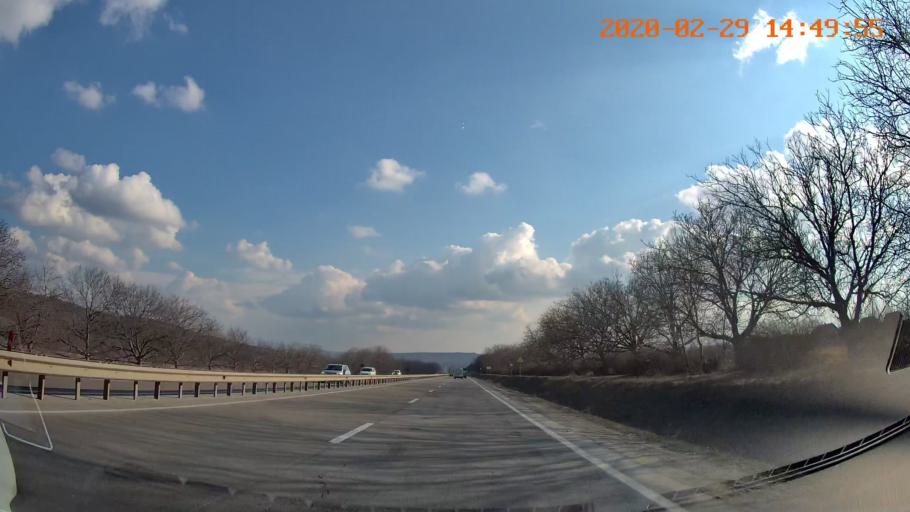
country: MD
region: Chisinau
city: Cricova
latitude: 47.1951
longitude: 28.7789
